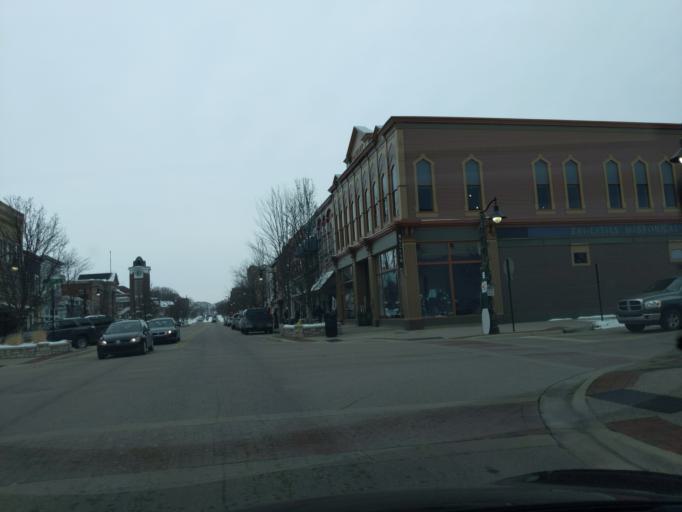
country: US
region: Michigan
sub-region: Ottawa County
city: Grand Haven
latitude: 43.0640
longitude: -86.2311
